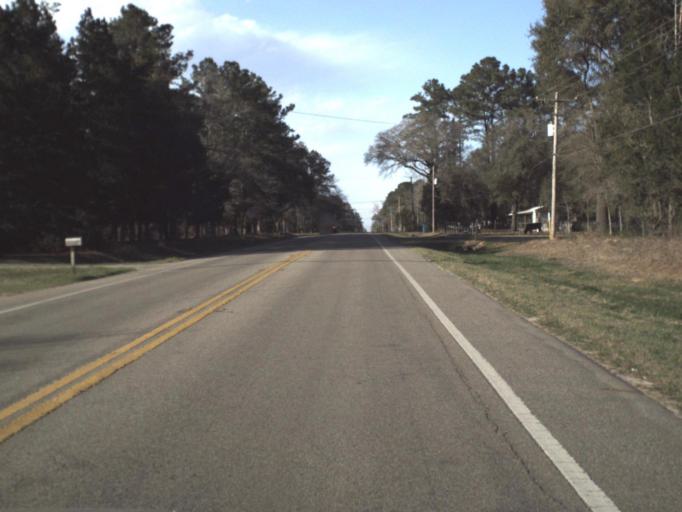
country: US
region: Florida
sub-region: Jackson County
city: Marianna
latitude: 30.7365
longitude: -85.2302
